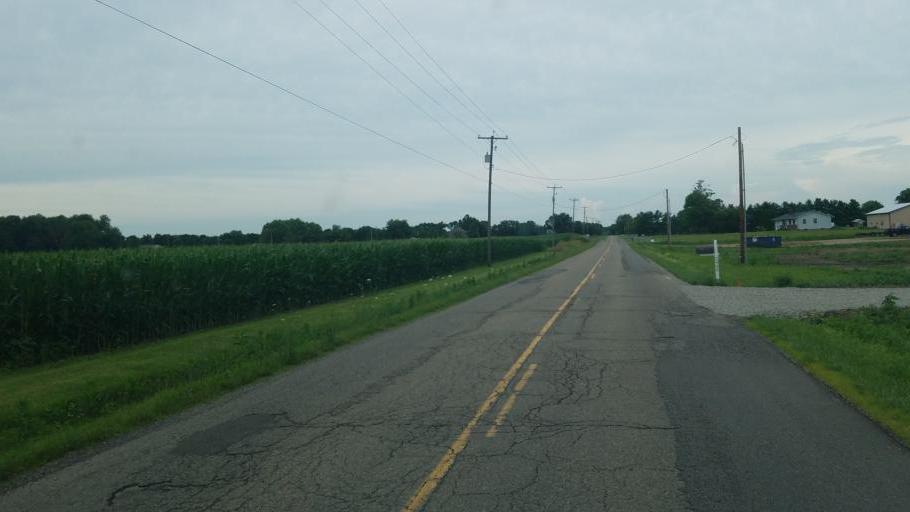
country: US
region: Ohio
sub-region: Knox County
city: Centerburg
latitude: 40.2793
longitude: -82.6902
